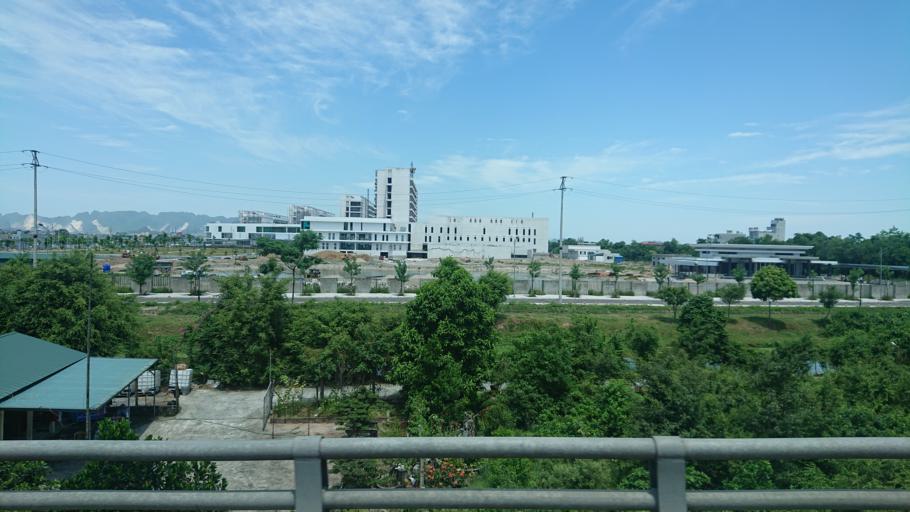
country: VN
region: Ha Nam
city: Thanh Pho Phu Ly
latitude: 20.5415
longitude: 105.9476
